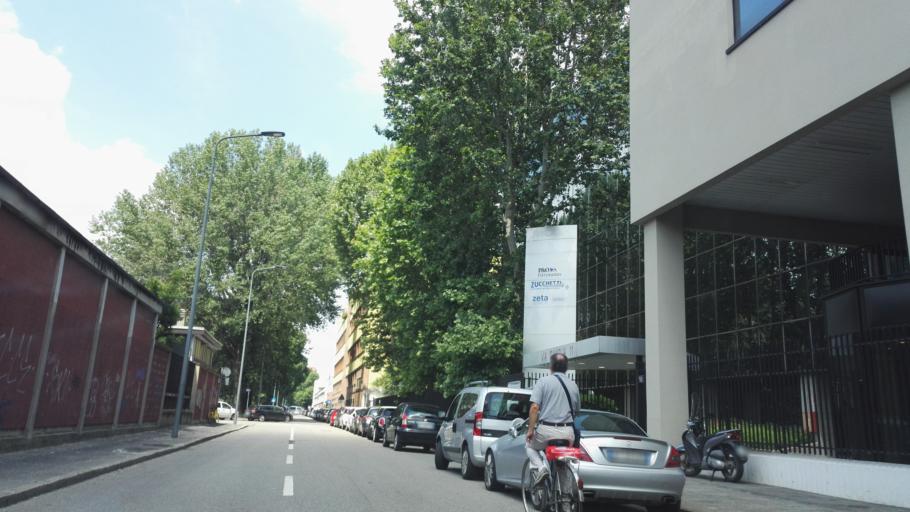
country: IT
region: Lombardy
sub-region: Citta metropolitana di Milano
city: Chiaravalle
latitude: 45.4409
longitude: 9.2307
